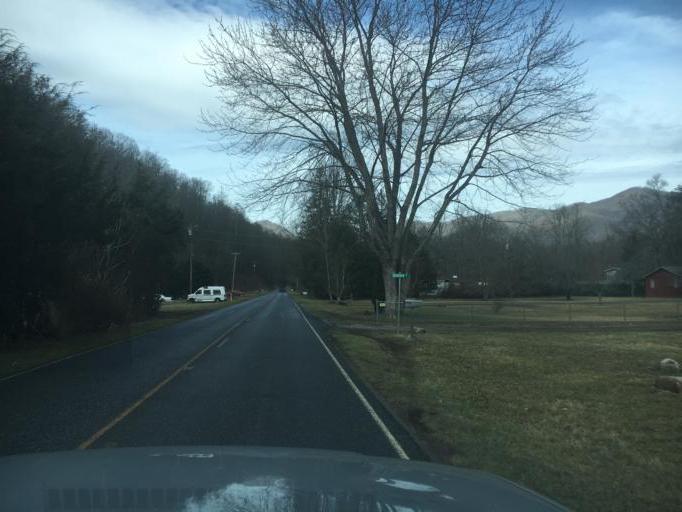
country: US
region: North Carolina
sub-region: Haywood County
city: Canton
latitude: 35.4301
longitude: -82.8134
